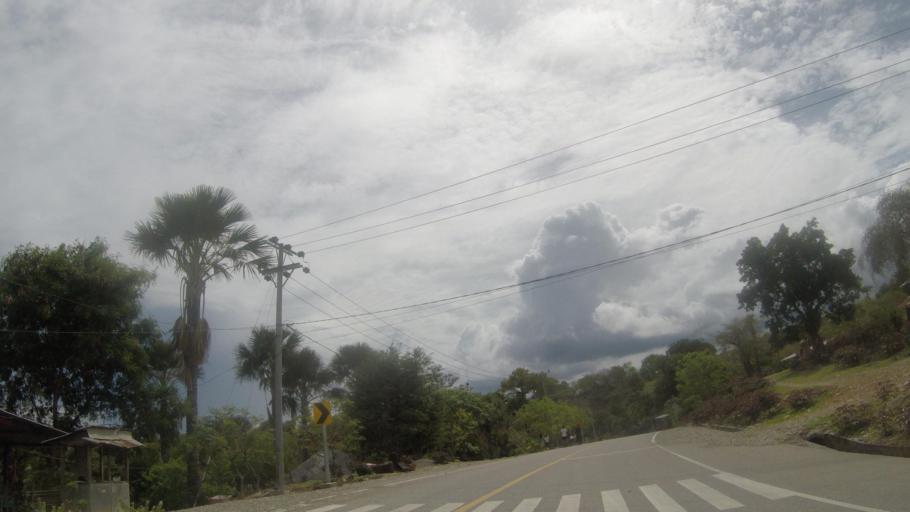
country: TL
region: Baucau
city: Baucau
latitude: -8.4784
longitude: 126.5907
